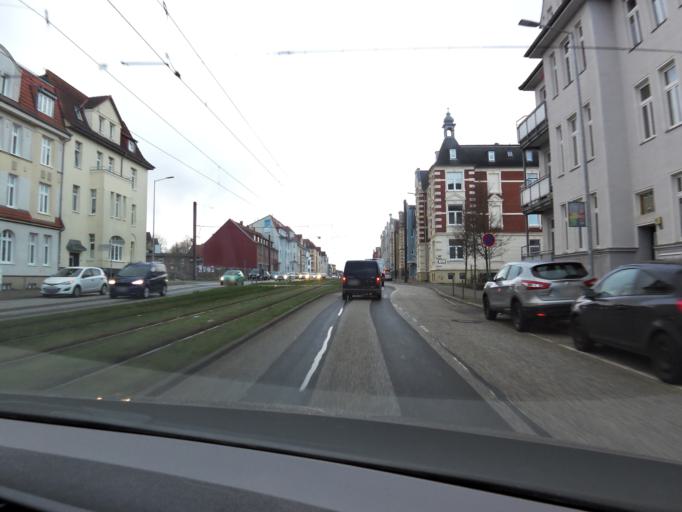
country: DE
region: Mecklenburg-Vorpommern
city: Weststadt
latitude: 53.6364
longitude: 11.3985
